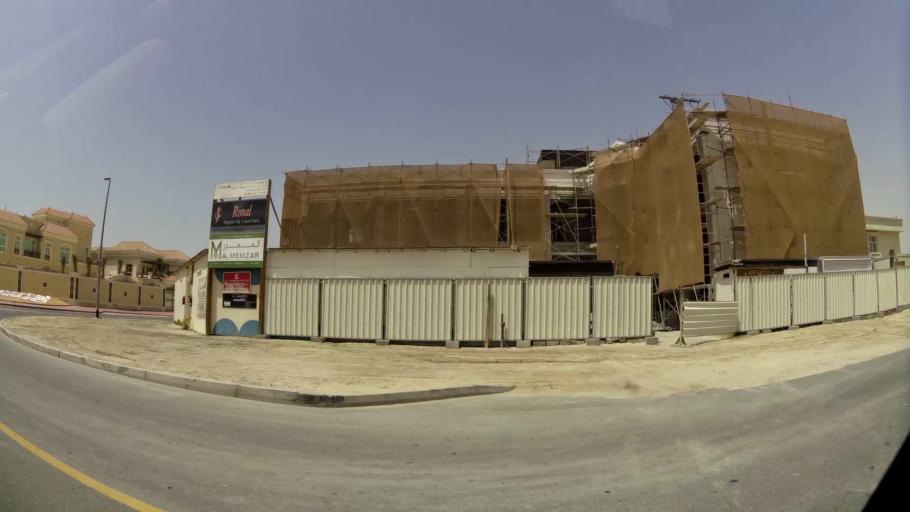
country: AE
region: Dubai
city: Dubai
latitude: 25.1353
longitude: 55.2026
